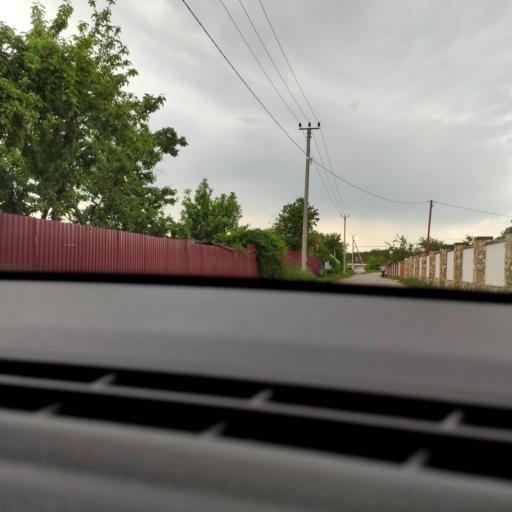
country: RU
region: Samara
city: Podstepki
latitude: 53.5126
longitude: 49.0717
